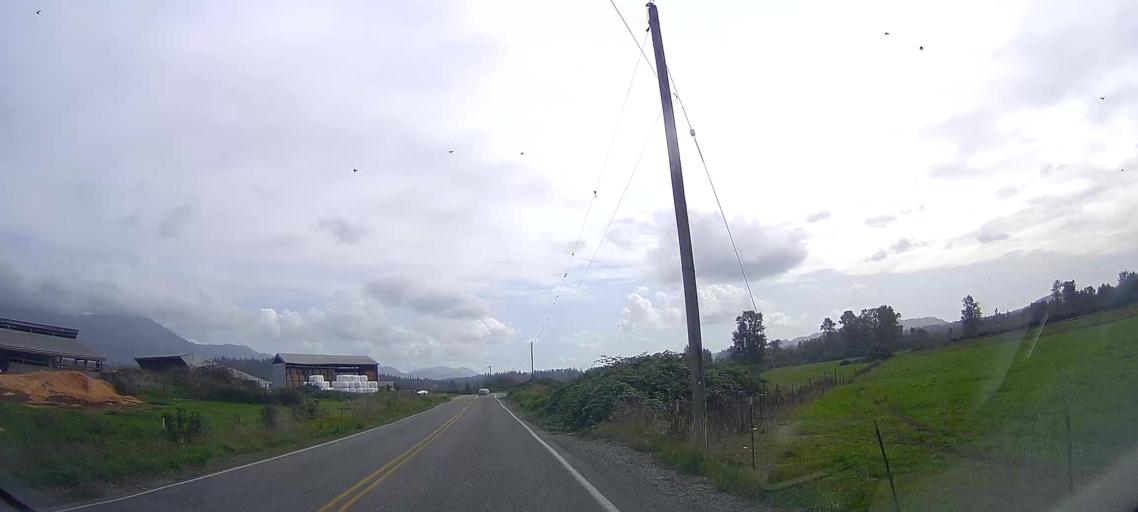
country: US
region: Washington
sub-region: Skagit County
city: Clear Lake
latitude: 48.4667
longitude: -122.2746
